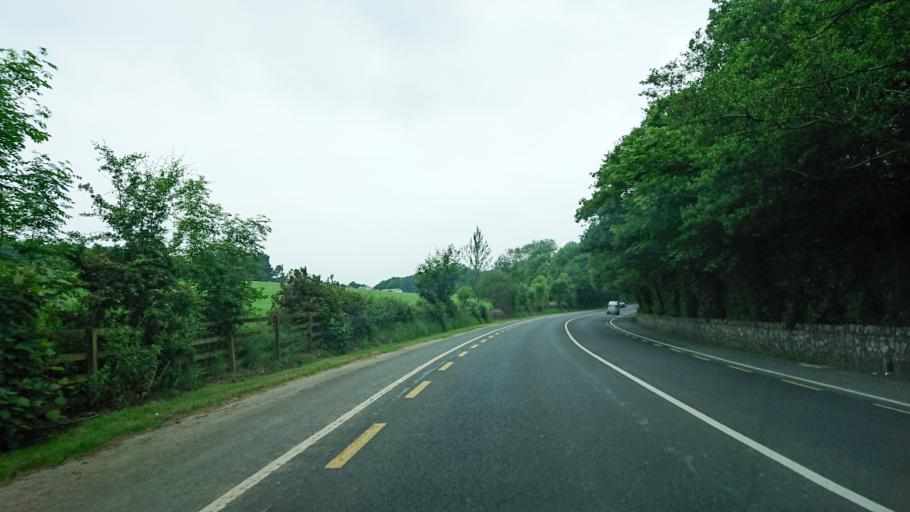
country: IE
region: Munster
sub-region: Waterford
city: Waterford
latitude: 52.2149
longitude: -7.1245
